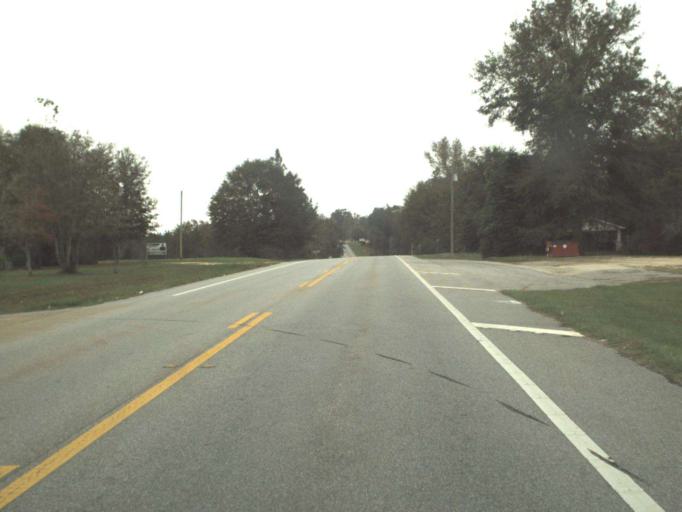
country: US
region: Alabama
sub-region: Escambia County
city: Atmore
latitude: 30.9527
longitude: -87.4868
